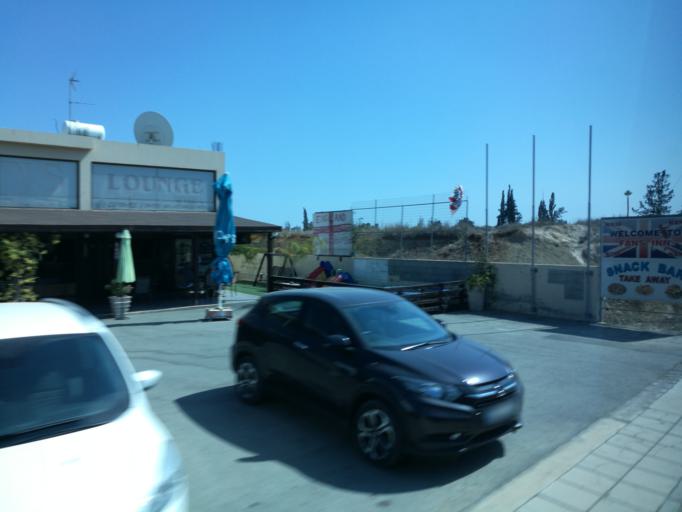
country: CY
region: Ammochostos
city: Acheritou
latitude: 35.0836
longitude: 33.8770
